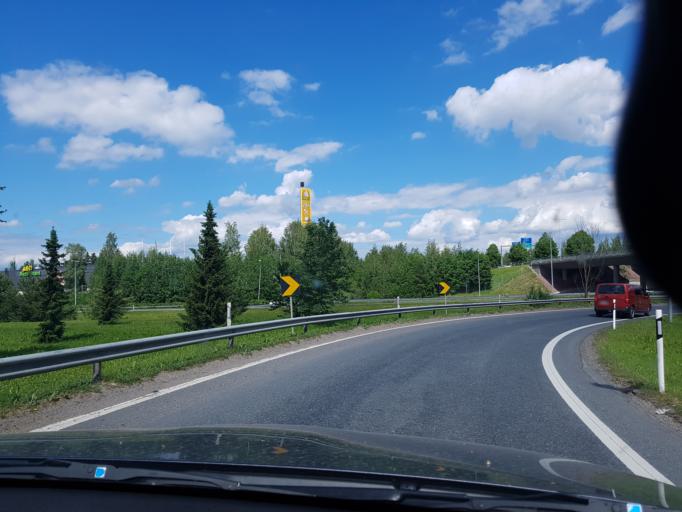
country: FI
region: Haeme
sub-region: Haemeenlinna
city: Haemeenlinna
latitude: 61.0118
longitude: 24.4166
